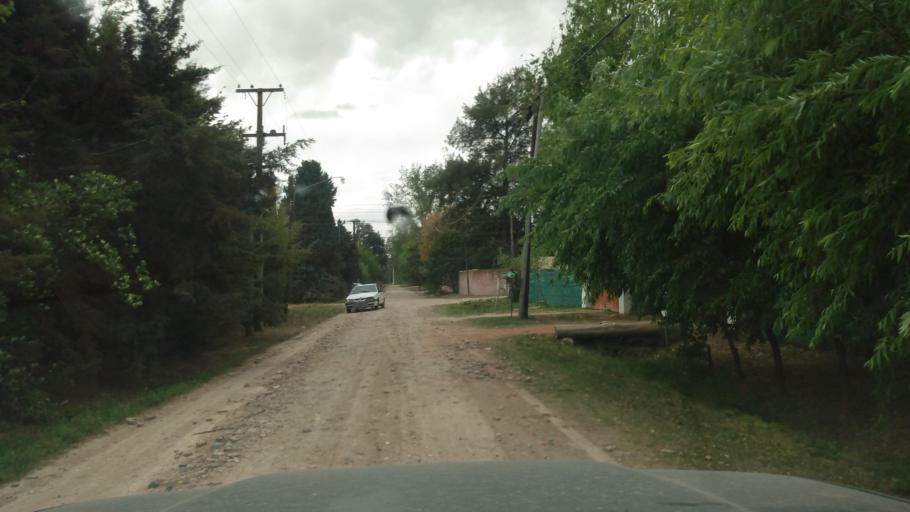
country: AR
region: Buenos Aires
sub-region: Partido de Lujan
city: Lujan
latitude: -34.5889
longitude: -59.1340
